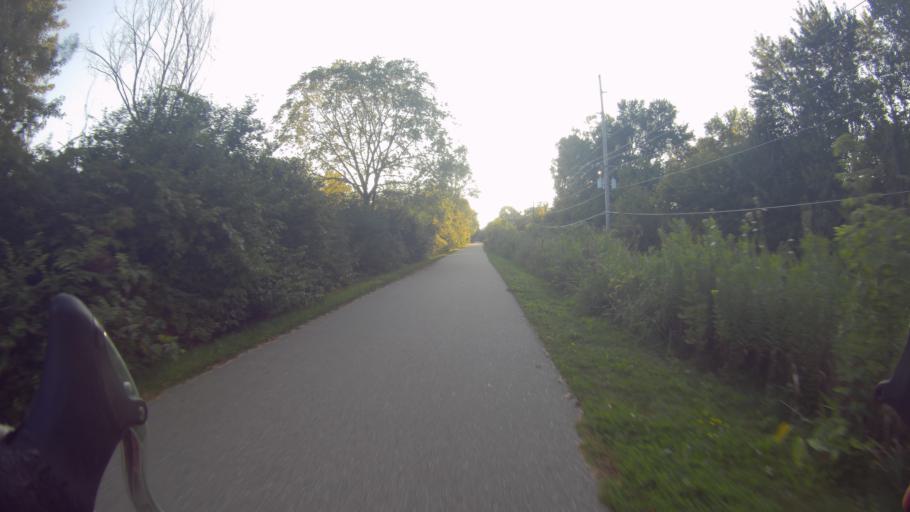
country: US
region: Wisconsin
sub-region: Dane County
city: Shorewood Hills
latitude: 43.0245
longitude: -89.4557
